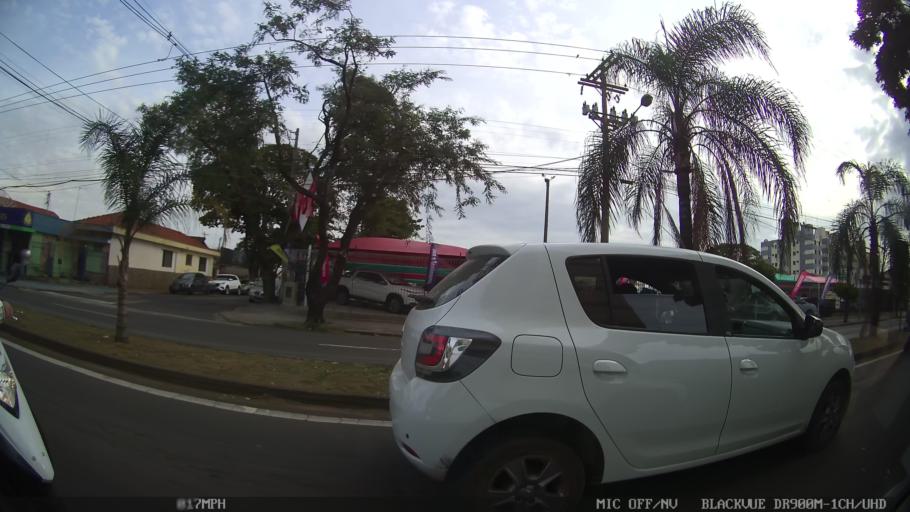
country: BR
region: Sao Paulo
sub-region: Piracicaba
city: Piracicaba
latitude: -22.7418
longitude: -47.6412
